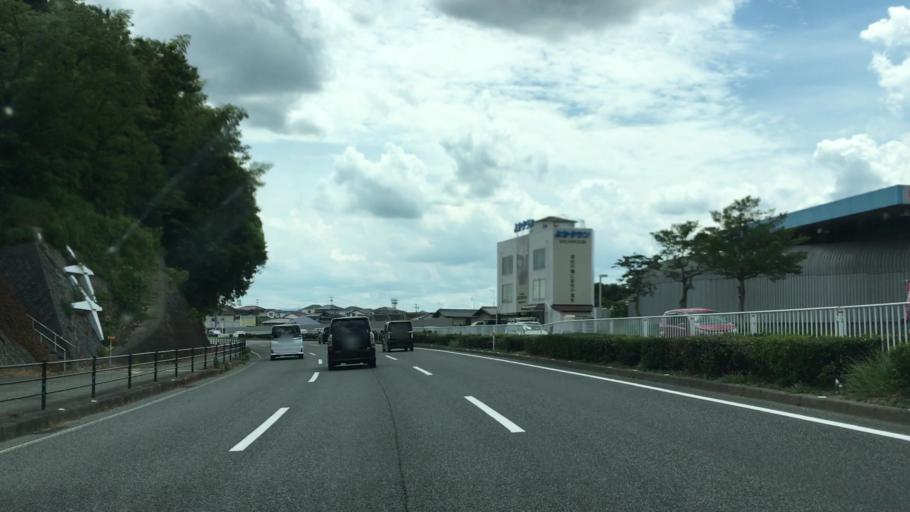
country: JP
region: Fukuoka
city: Dazaifu
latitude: 33.4990
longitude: 130.5317
